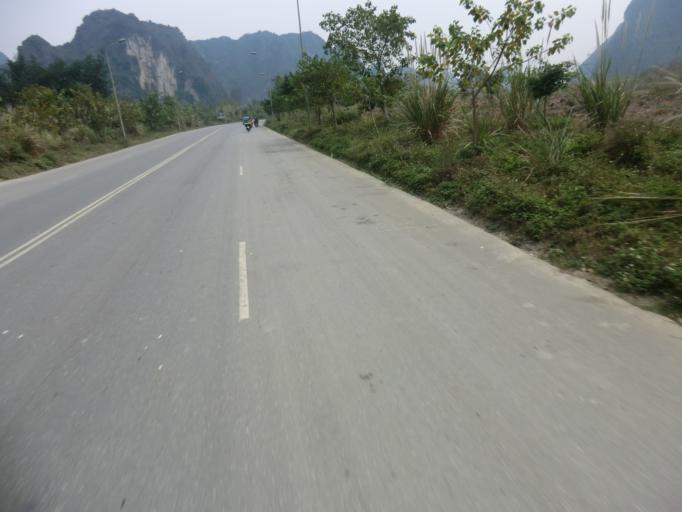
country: VN
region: Ninh Binh
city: Thi Tran Thien Ton
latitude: 20.2522
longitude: 105.9214
